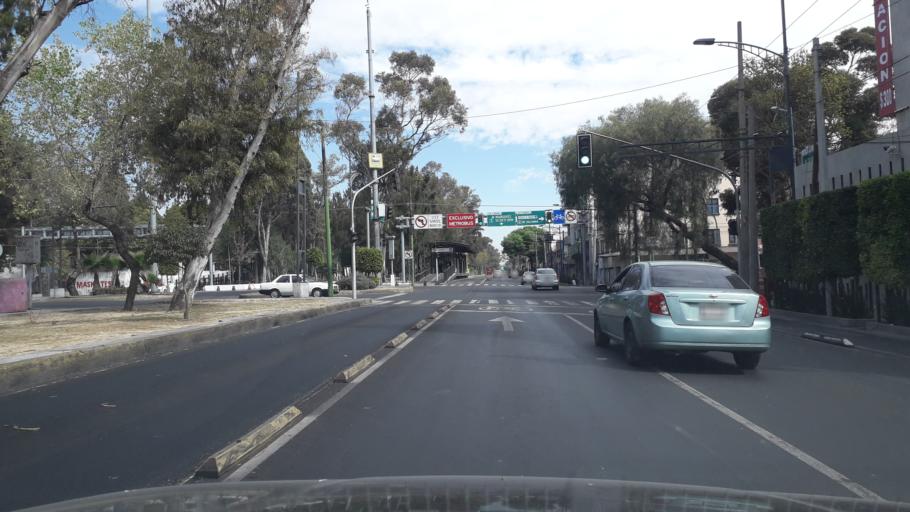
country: MX
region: Mexico City
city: Gustavo A. Madero
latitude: 19.4700
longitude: -99.1015
